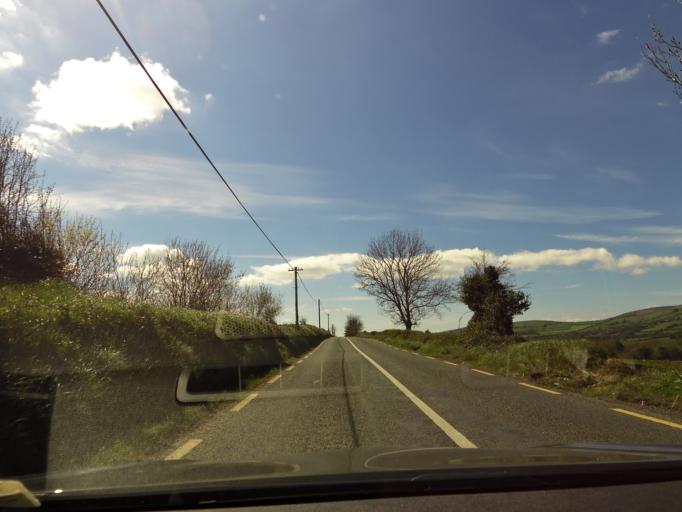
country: IE
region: Leinster
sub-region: Wicklow
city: Aughrim
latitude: 52.8162
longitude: -6.3943
